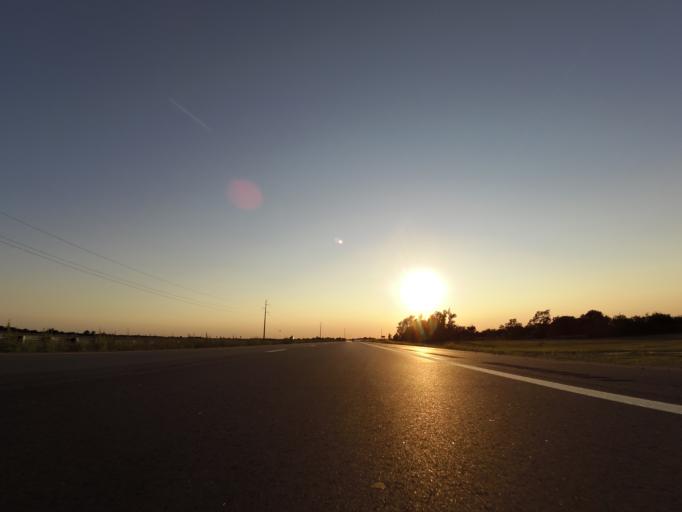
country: US
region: Kansas
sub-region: Reno County
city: South Hutchinson
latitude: 38.0136
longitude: -97.9679
